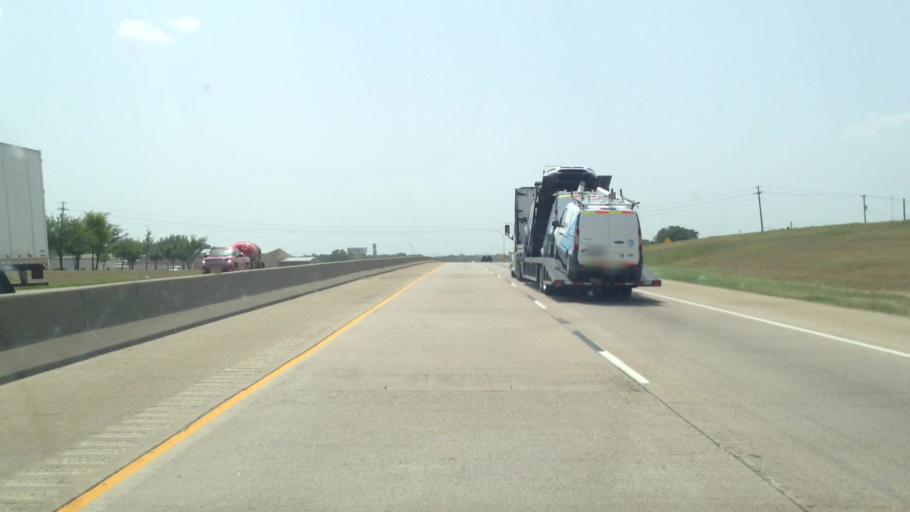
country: US
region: Texas
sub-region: Hopkins County
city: Sulphur Springs
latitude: 33.1164
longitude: -95.5983
